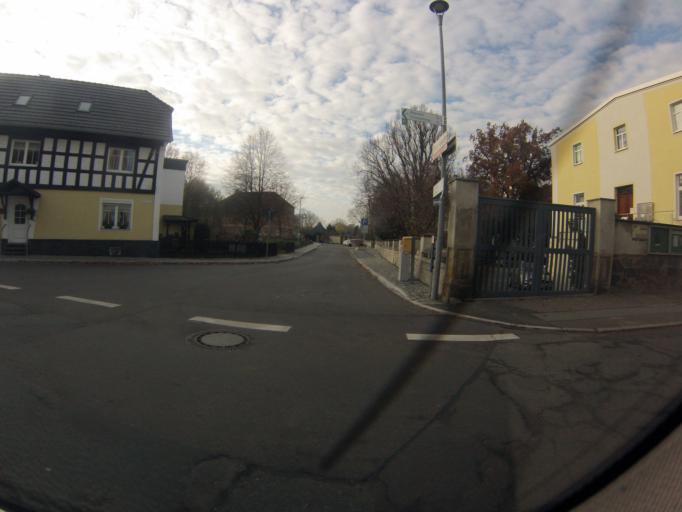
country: DE
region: Thuringia
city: Ponitz
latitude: 50.8561
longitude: 12.4233
